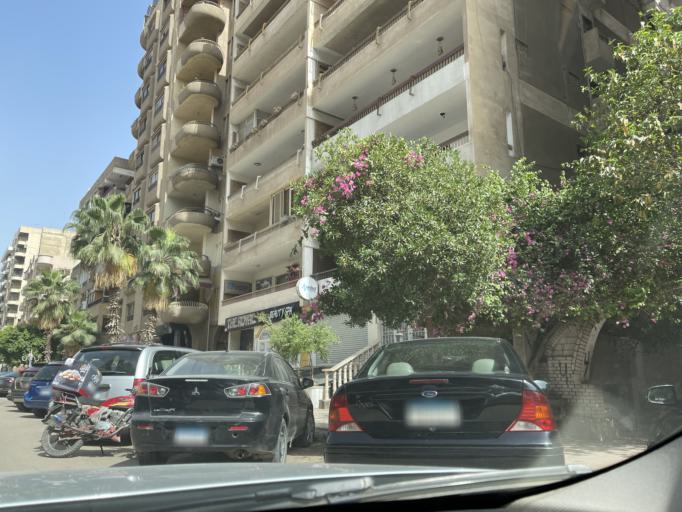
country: EG
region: Muhafazat al Qahirah
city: Cairo
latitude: 30.0601
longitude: 31.3514
